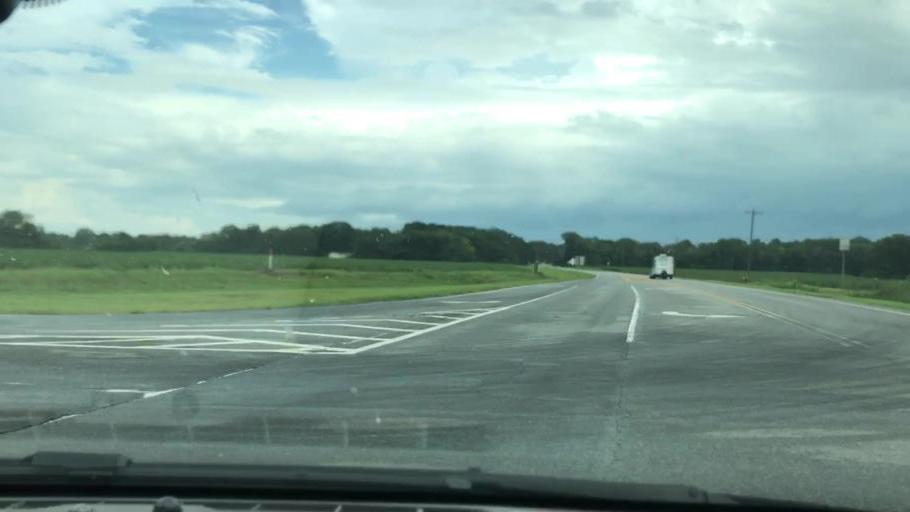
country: US
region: Georgia
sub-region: Early County
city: Blakely
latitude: 31.3898
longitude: -84.9442
